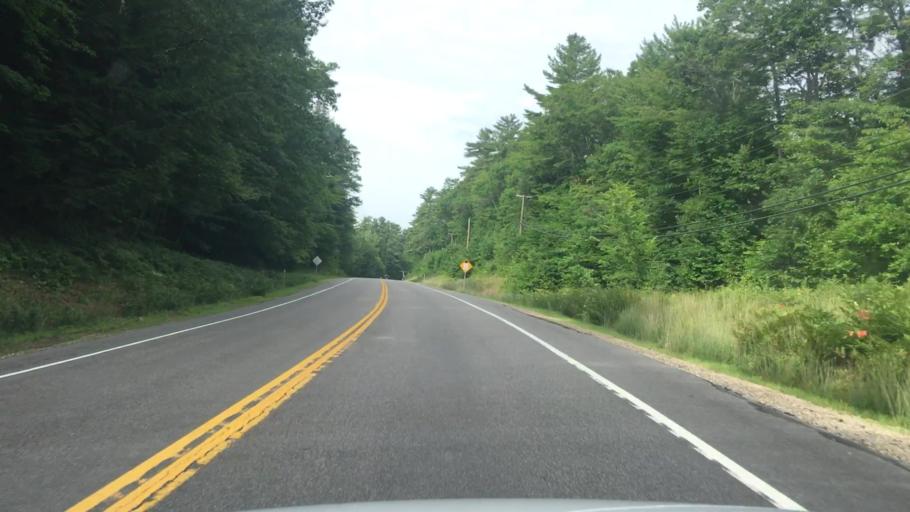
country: US
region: New Hampshire
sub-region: Carroll County
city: Tamworth
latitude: 43.8278
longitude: -71.2965
